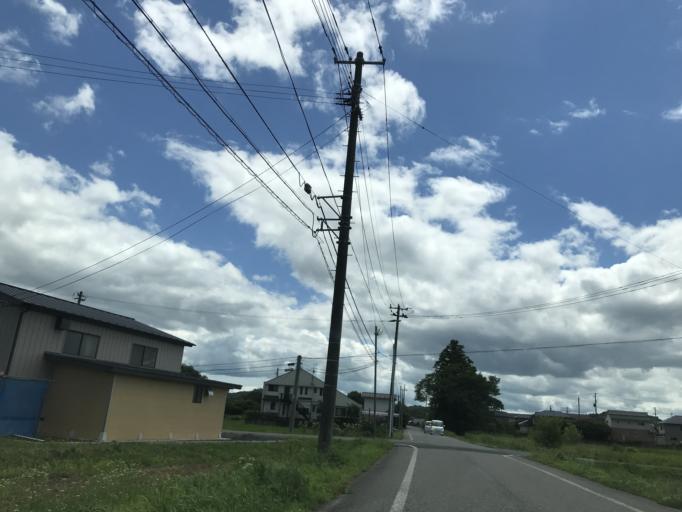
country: JP
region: Iwate
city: Ichinoseki
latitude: 38.9350
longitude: 141.0945
